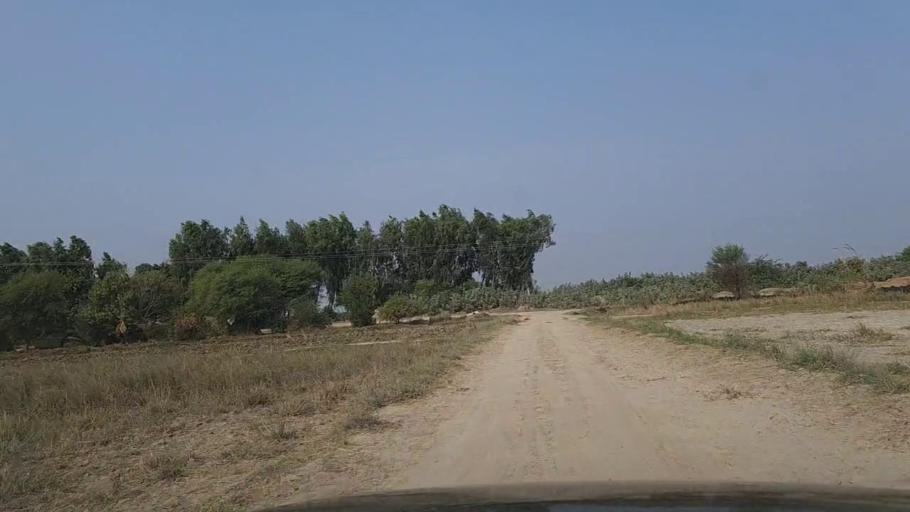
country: PK
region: Sindh
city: Thatta
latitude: 24.7558
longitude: 67.7992
